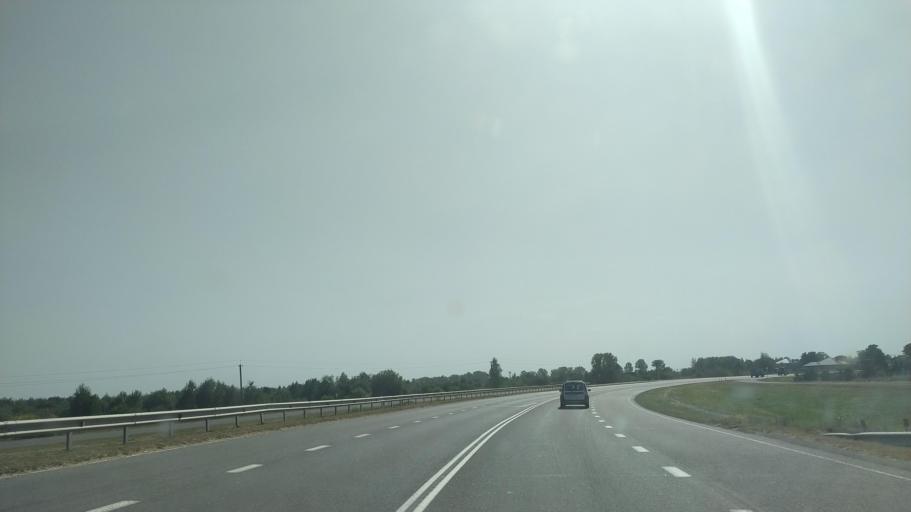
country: BY
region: Brest
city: Byaroza
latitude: 52.4877
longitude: 24.9696
